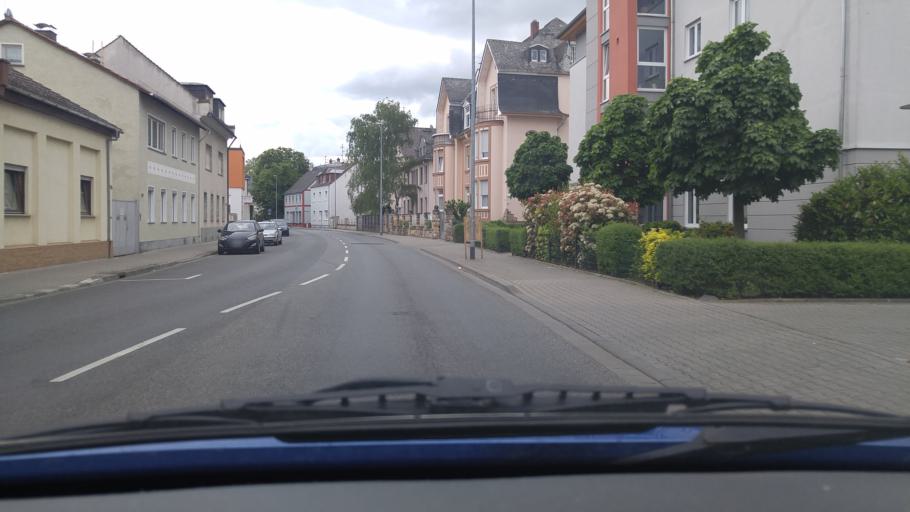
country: DE
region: Rheinland-Pfalz
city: Mainz
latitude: 50.0005
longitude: 8.3030
